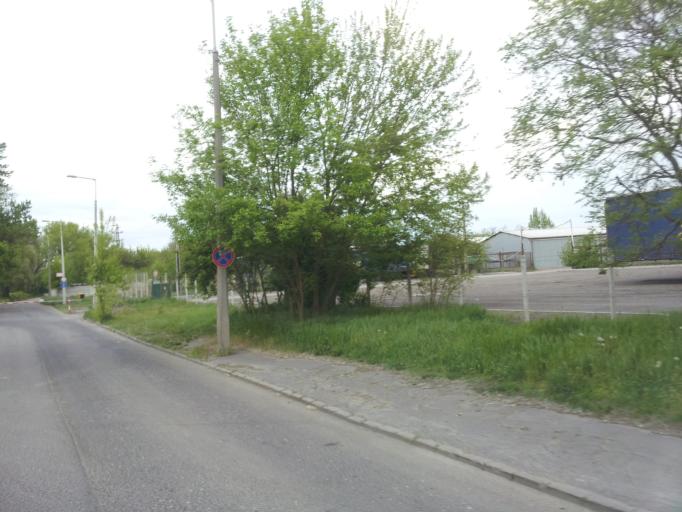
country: HU
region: Budapest
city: Budapest XV. keruelet
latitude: 47.5868
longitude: 19.1331
